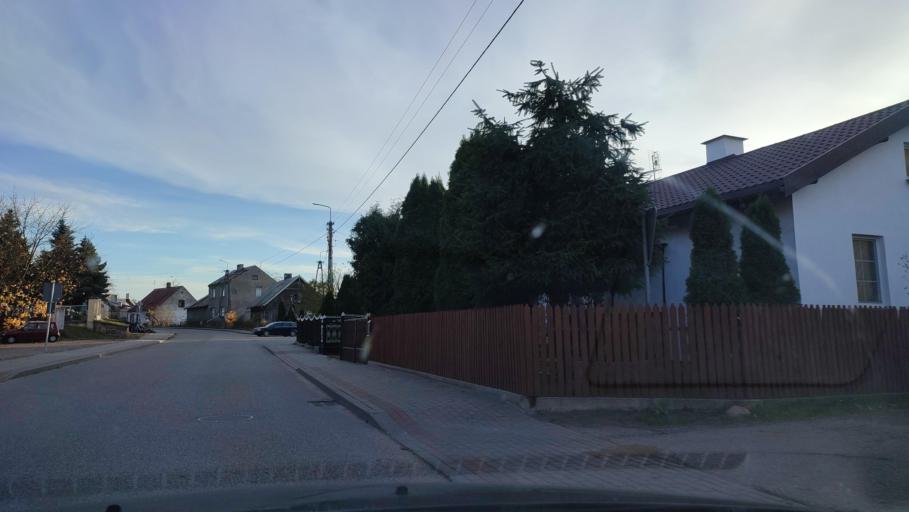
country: PL
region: Masovian Voivodeship
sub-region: Powiat mlawski
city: Dzierzgowo
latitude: 53.3137
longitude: 20.6732
